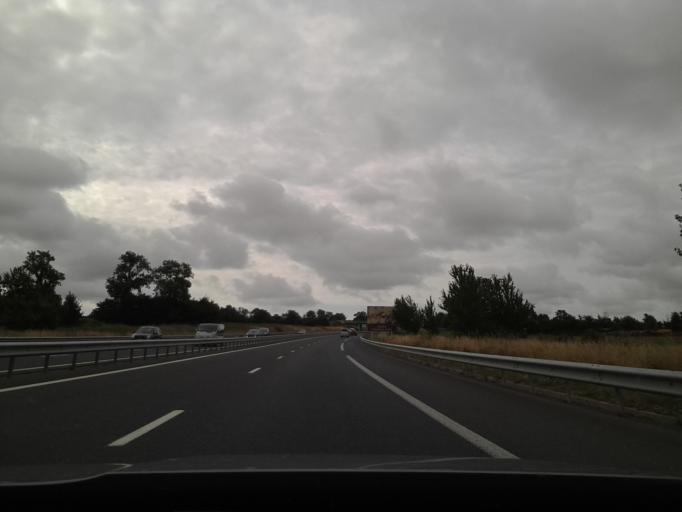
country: FR
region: Lower Normandy
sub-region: Departement du Calvados
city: Bayeux
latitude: 49.2775
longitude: -0.7387
